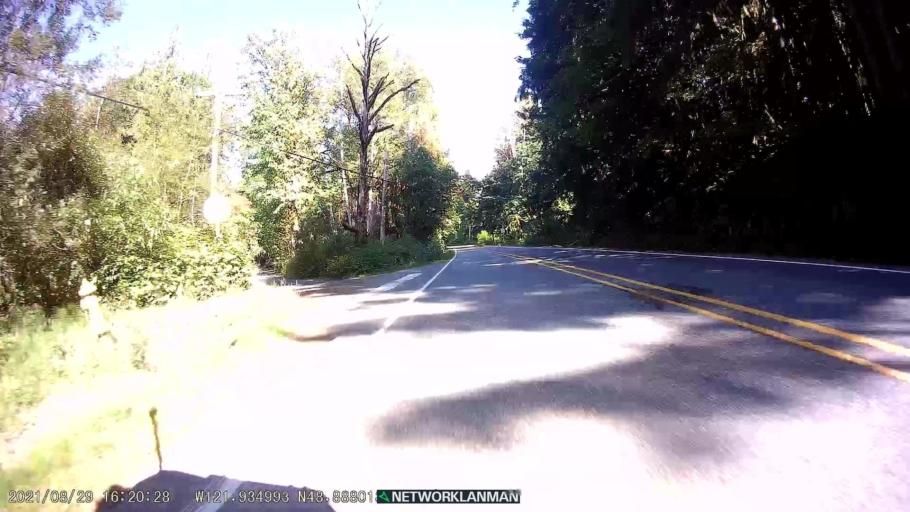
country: US
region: Washington
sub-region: Whatcom County
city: Peaceful Valley
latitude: 48.8879
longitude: -121.9354
